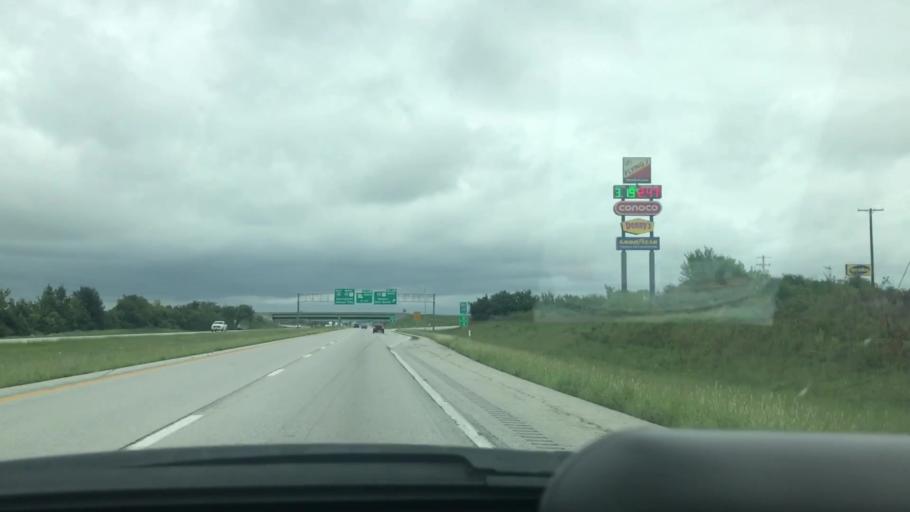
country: US
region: Missouri
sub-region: Jasper County
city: Duquesne
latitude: 37.0585
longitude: -94.4353
